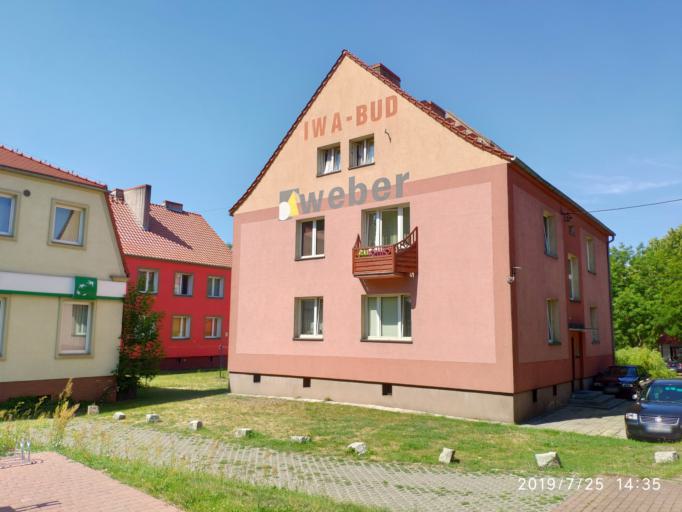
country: PL
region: Lubusz
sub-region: Powiat krosnienski
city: Krosno Odrzanskie
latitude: 52.0546
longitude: 15.0993
